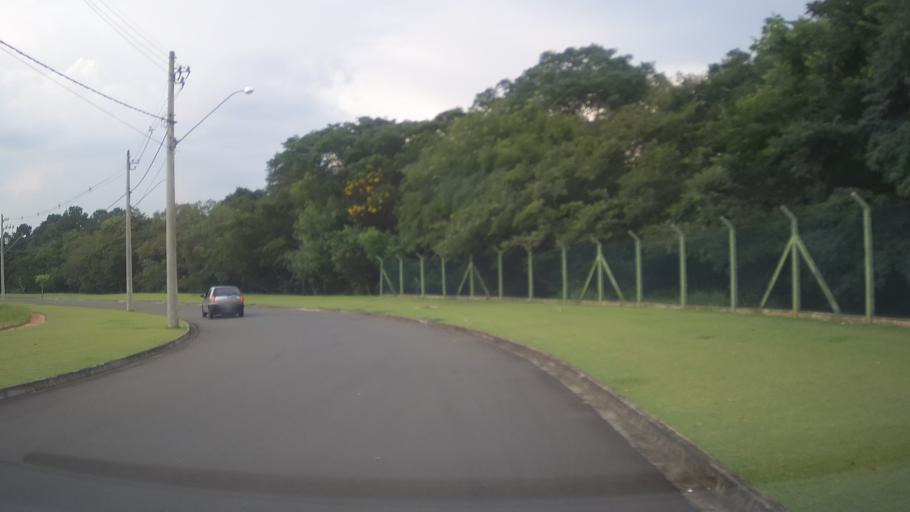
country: BR
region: Sao Paulo
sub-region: Jundiai
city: Jundiai
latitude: -23.1884
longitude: -46.9727
